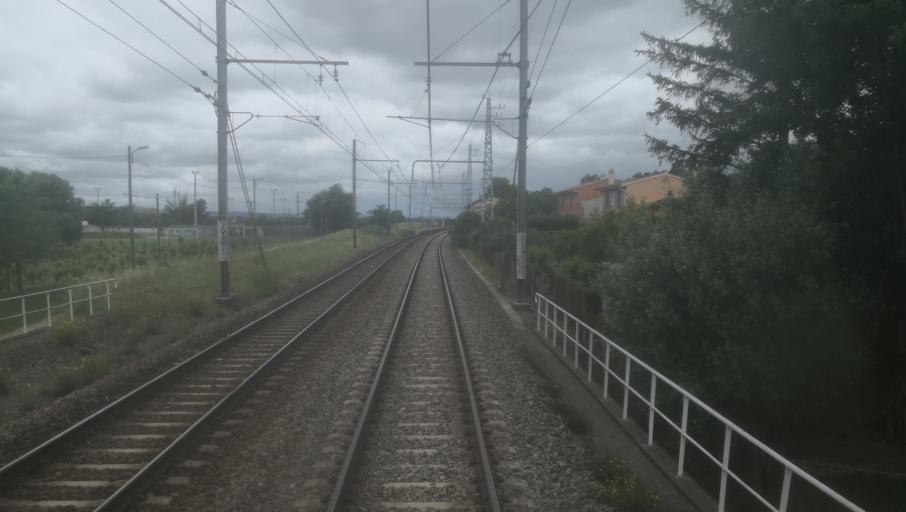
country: FR
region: Midi-Pyrenees
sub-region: Departement de la Haute-Garonne
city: Villenouvelle
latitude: 43.4323
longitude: 1.6627
